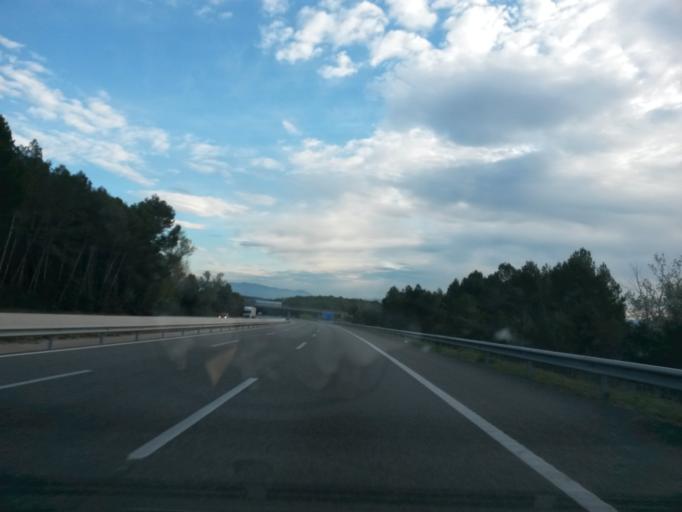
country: ES
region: Catalonia
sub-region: Provincia de Girona
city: Bascara
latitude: 42.1379
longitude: 2.9176
